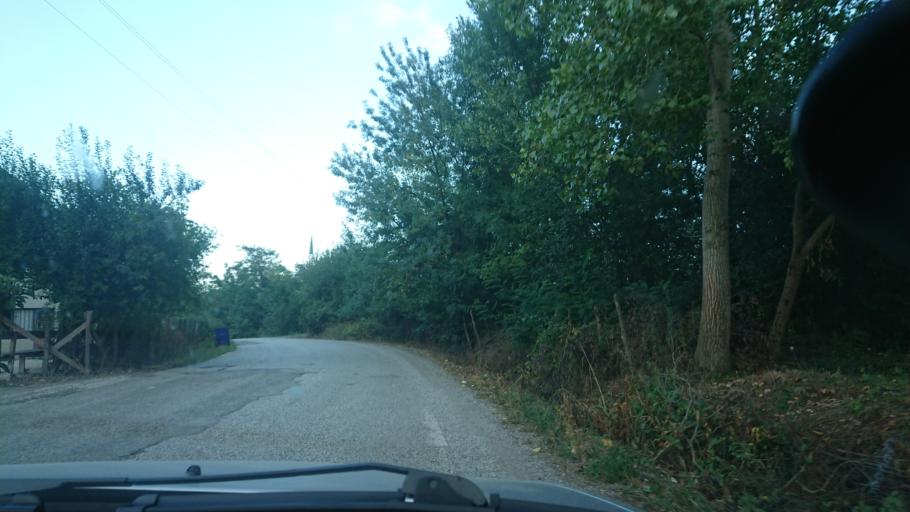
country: TR
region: Samsun
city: Tekkekoy
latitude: 41.1721
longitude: 36.5362
